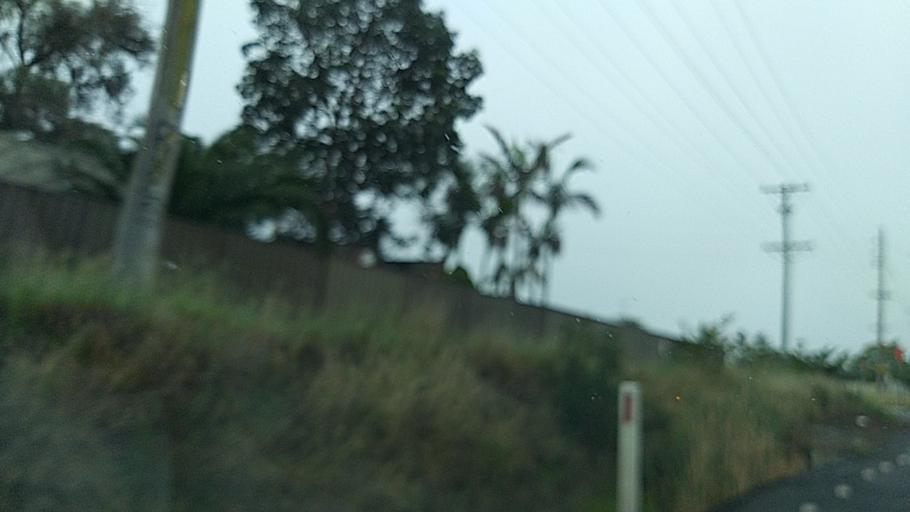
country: AU
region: New South Wales
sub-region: Penrith Municipality
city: Kingswood Park
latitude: -33.7823
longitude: 150.7078
